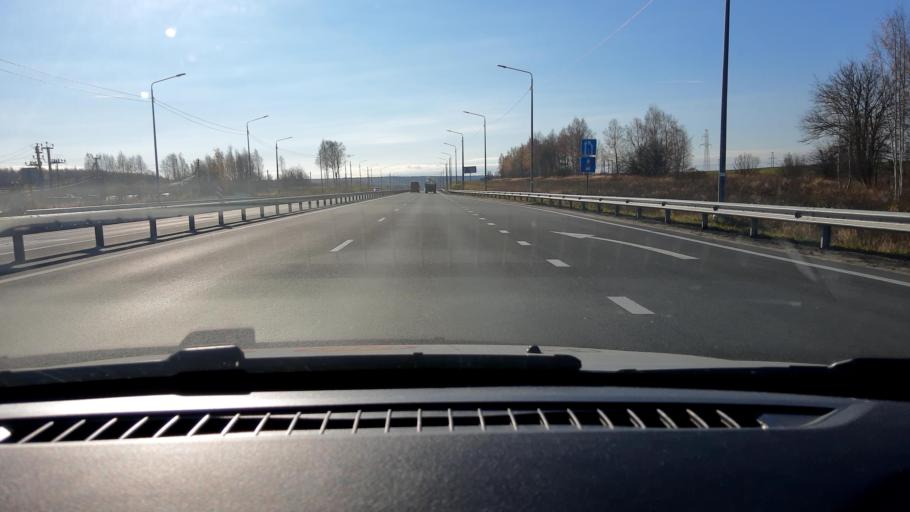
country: RU
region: Nizjnij Novgorod
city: Burevestnik
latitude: 56.1029
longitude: 43.9181
